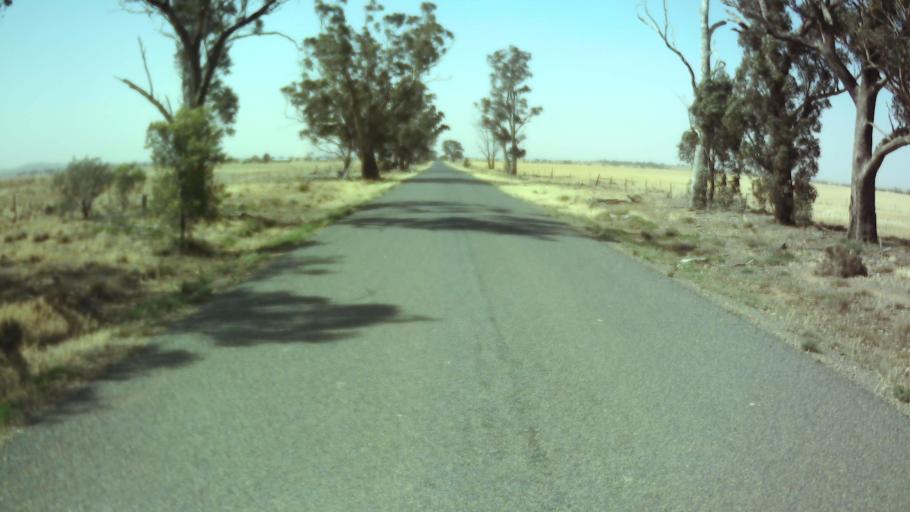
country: AU
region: New South Wales
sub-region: Weddin
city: Grenfell
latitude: -33.8870
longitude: 147.9233
